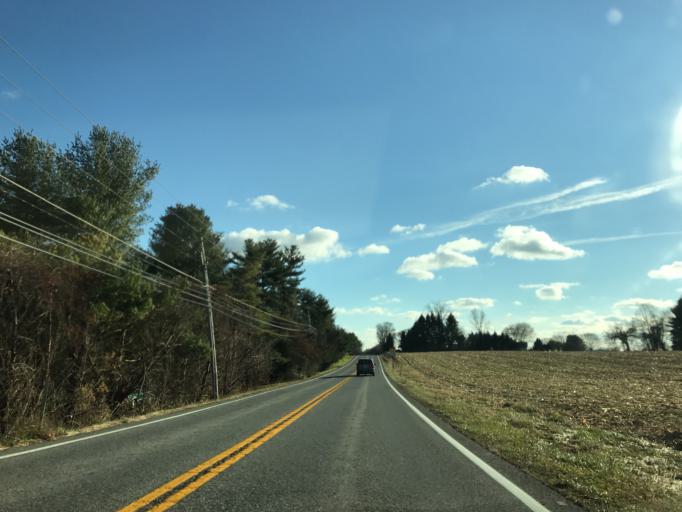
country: US
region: Maryland
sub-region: Harford County
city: Jarrettsville
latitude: 39.5761
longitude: -76.4999
